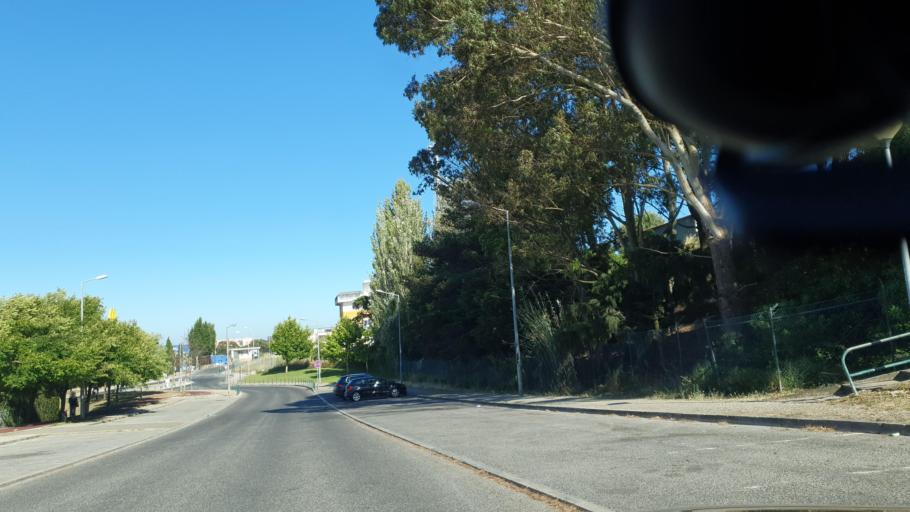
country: PT
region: Lisbon
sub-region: Sintra
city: Queluz
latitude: 38.7533
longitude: -9.2706
